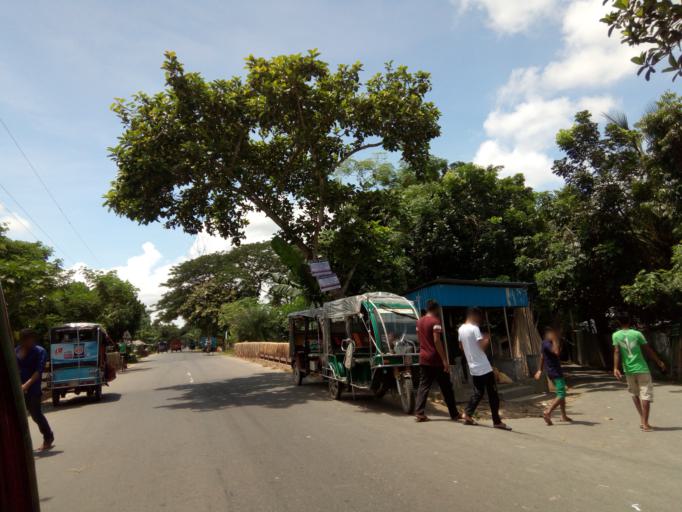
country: BD
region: Dhaka
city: Tungipara
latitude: 22.9107
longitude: 89.8734
